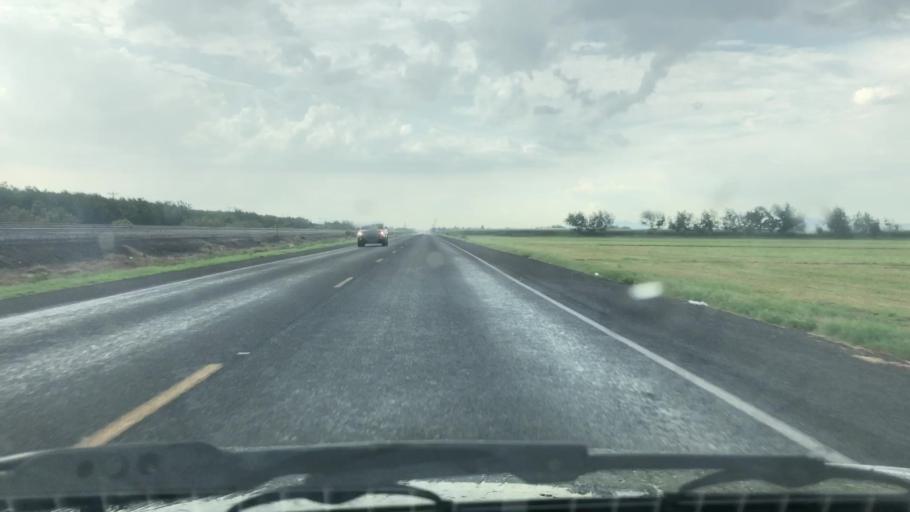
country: US
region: New Mexico
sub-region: Dona Ana County
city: Mesquite
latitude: 32.1471
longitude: -106.6856
